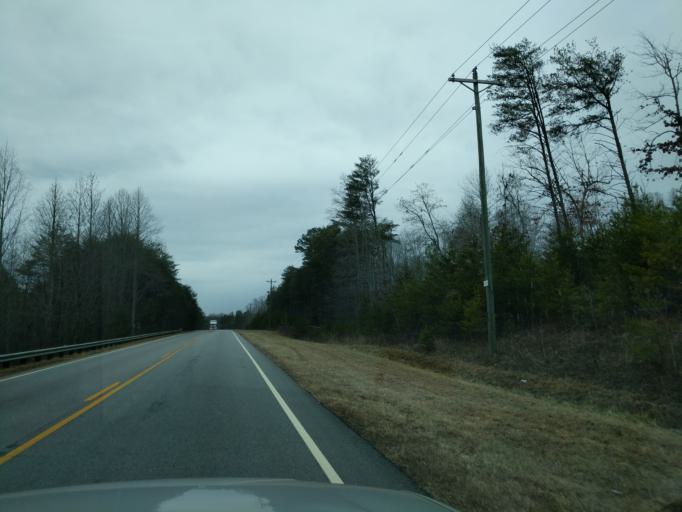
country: US
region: South Carolina
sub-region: Greenville County
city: Slater-Marietta
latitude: 35.0794
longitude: -82.5031
